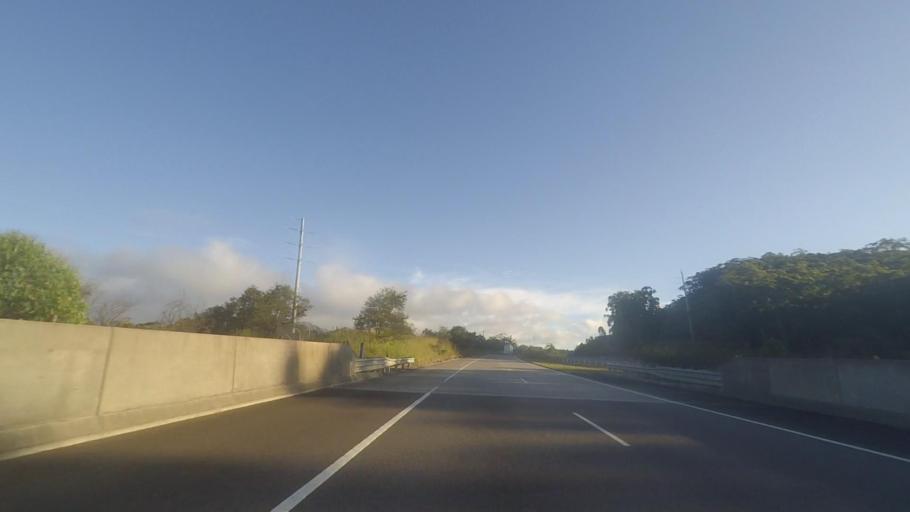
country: AU
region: New South Wales
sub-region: Great Lakes
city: Bulahdelah
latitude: -32.5034
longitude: 152.2109
